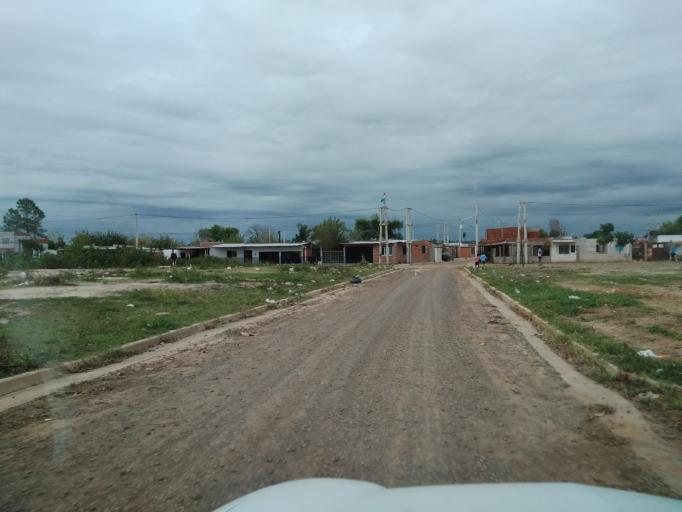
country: AR
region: Corrientes
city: Corrientes
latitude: -27.5008
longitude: -58.8043
